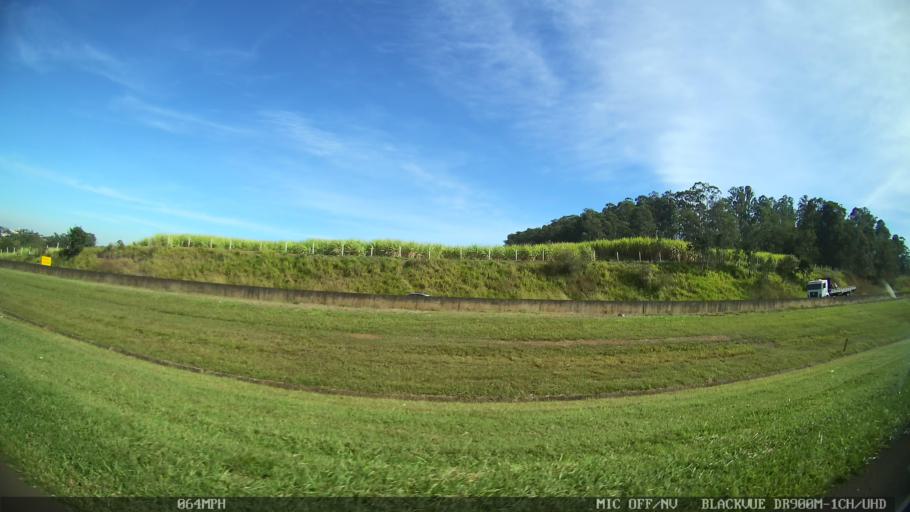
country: BR
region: Sao Paulo
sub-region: Araras
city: Araras
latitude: -22.3344
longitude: -47.3893
